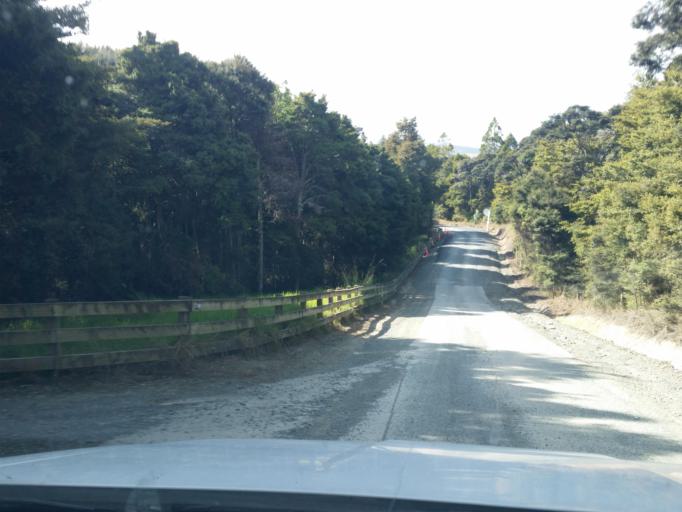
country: NZ
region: Auckland
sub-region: Auckland
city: Wellsford
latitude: -36.1633
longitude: 174.5523
